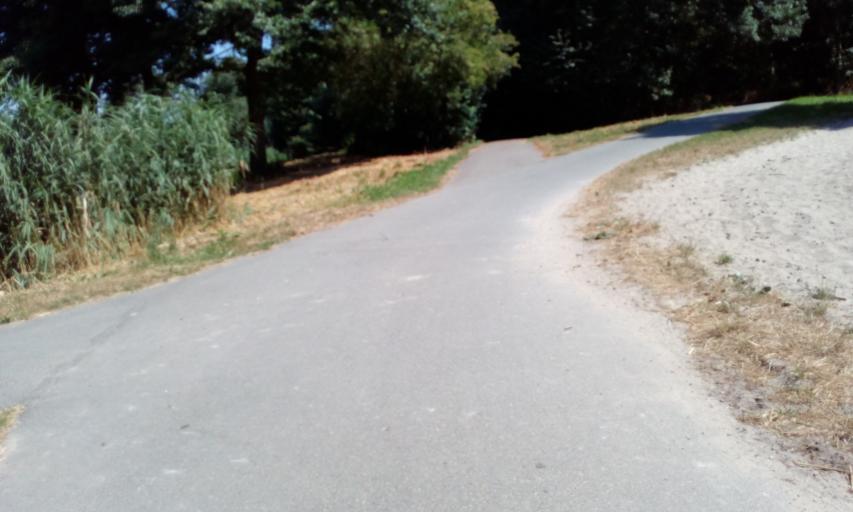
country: NL
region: South Holland
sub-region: Gemeente Capelle aan den IJssel
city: Capelle aan den IJssel
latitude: 51.9471
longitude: 4.5923
